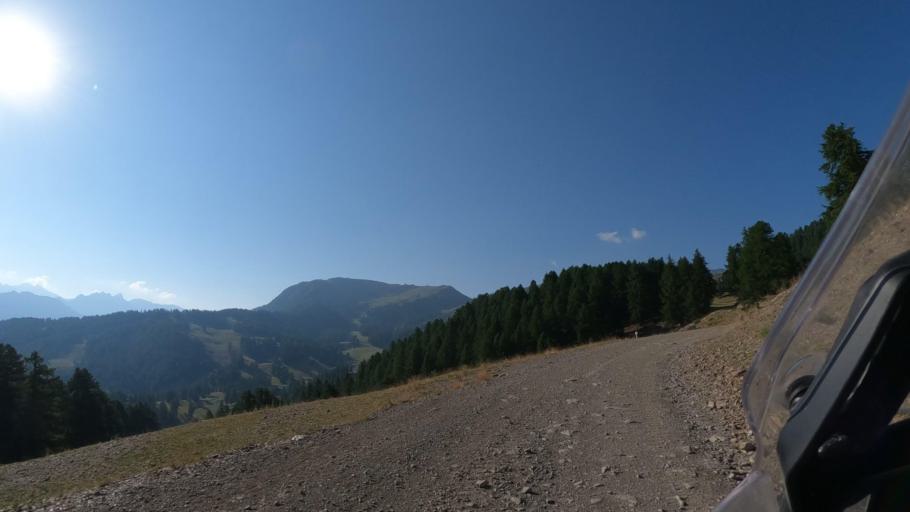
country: FR
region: Provence-Alpes-Cote d'Azur
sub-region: Departement des Hautes-Alpes
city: Guillestre
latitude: 44.6175
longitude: 6.6244
